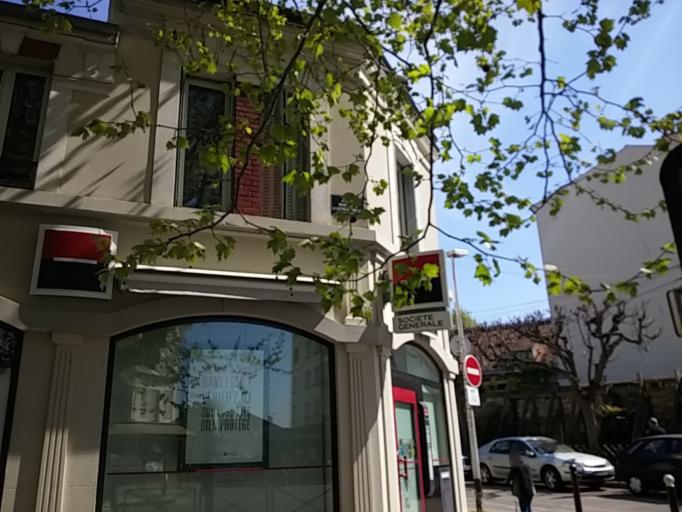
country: FR
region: Ile-de-France
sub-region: Departement du Val-de-Marne
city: Creteil
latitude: 48.7954
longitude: 2.4590
